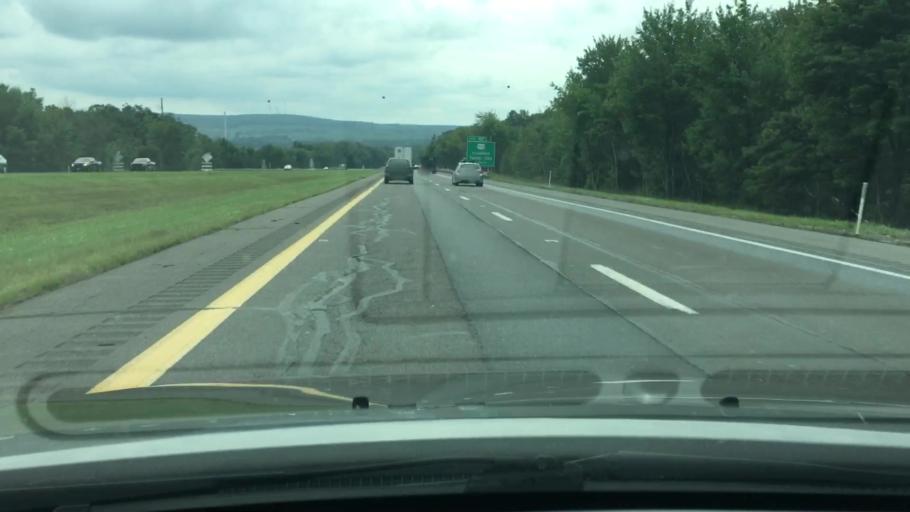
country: US
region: Pennsylvania
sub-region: Schuylkill County
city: Tremont
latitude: 40.6405
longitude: -76.4318
